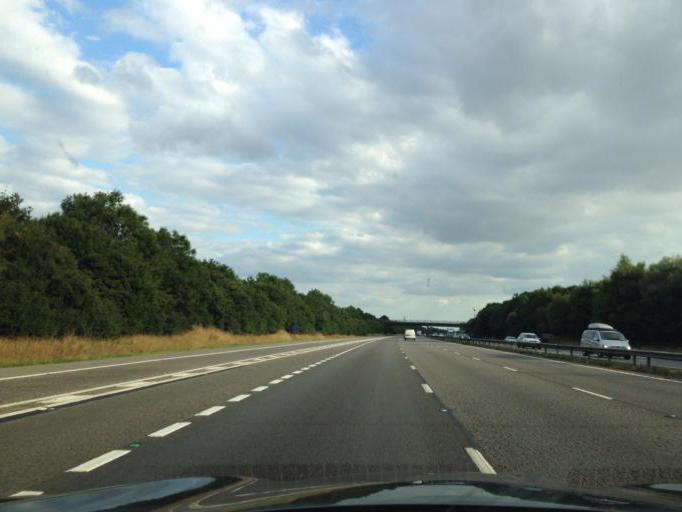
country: GB
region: England
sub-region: Oxfordshire
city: Banbury
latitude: 52.0681
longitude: -1.3102
